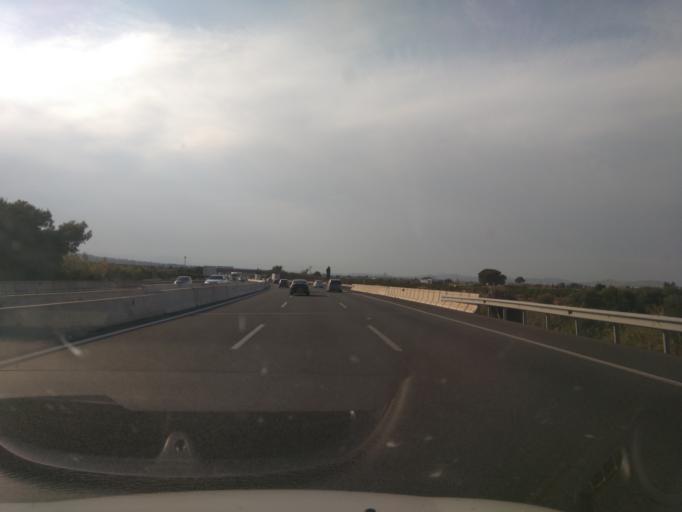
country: ES
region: Valencia
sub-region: Provincia de Valencia
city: Torrent
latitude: 39.4208
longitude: -0.5144
